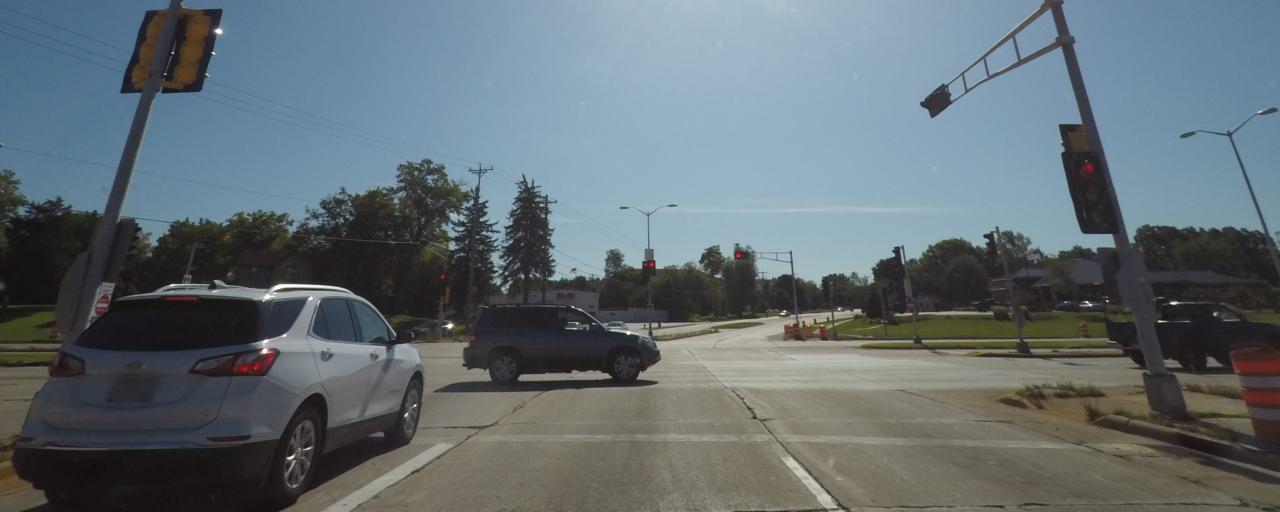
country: US
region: Wisconsin
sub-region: Waukesha County
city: Waukesha
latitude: 42.9966
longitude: -88.2017
